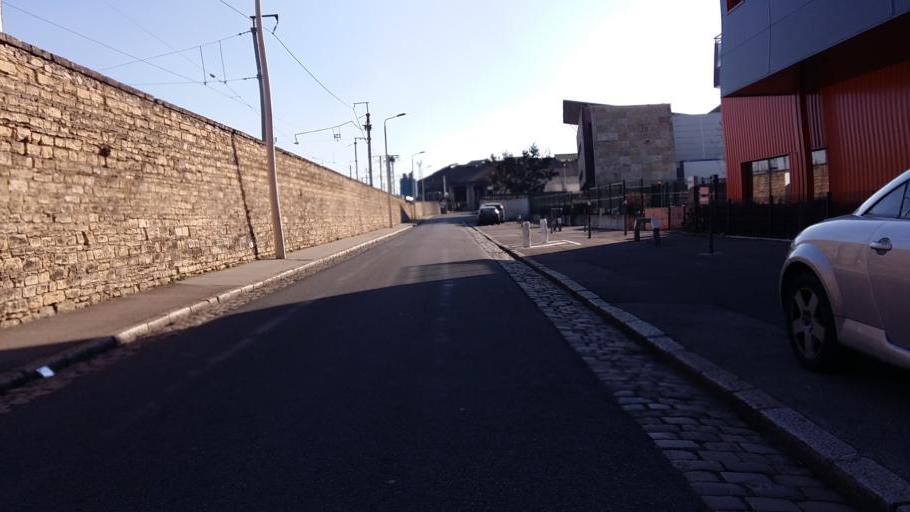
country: FR
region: Rhone-Alpes
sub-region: Departement du Rhone
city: Lyon
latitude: 45.7406
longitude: 4.8451
